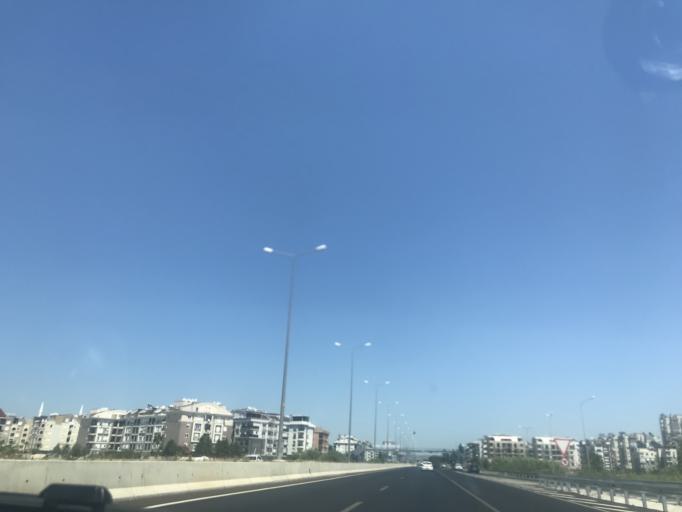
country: TR
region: Antalya
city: Cakirlar
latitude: 36.8496
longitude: 30.6025
